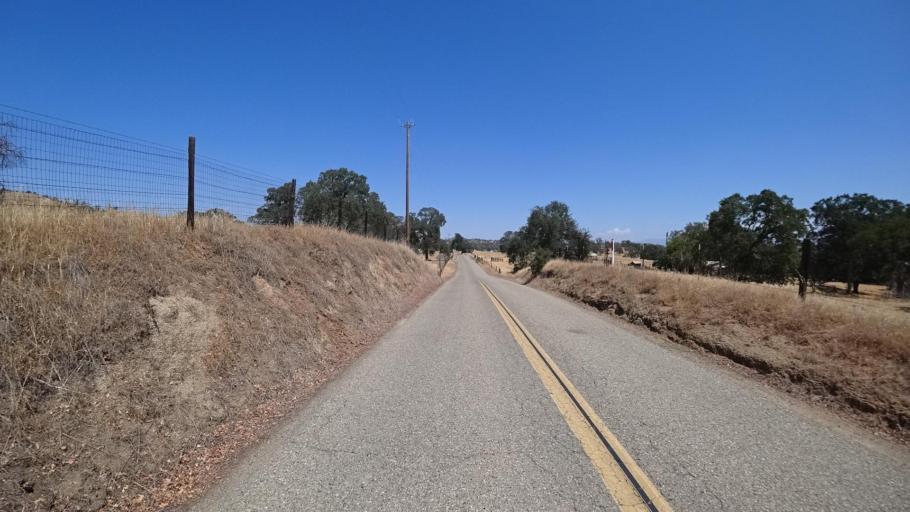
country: US
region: California
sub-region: Madera County
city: Yosemite Lakes
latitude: 37.2585
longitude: -119.9748
